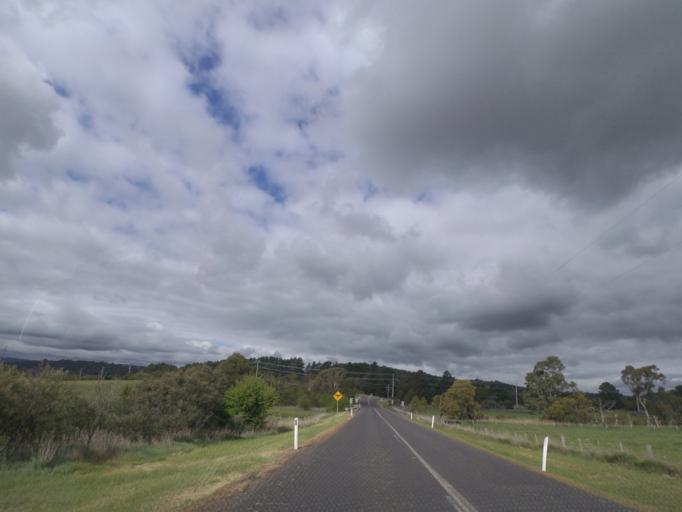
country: AU
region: Victoria
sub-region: Whittlesea
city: Whittlesea
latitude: -37.4742
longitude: 145.0224
